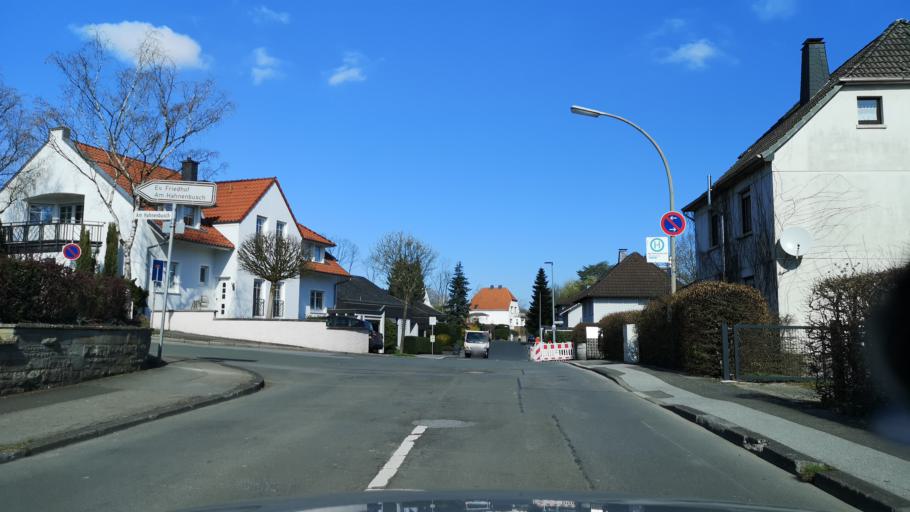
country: DE
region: North Rhine-Westphalia
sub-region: Regierungsbezirk Arnsberg
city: Menden
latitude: 51.4324
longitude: 7.7853
